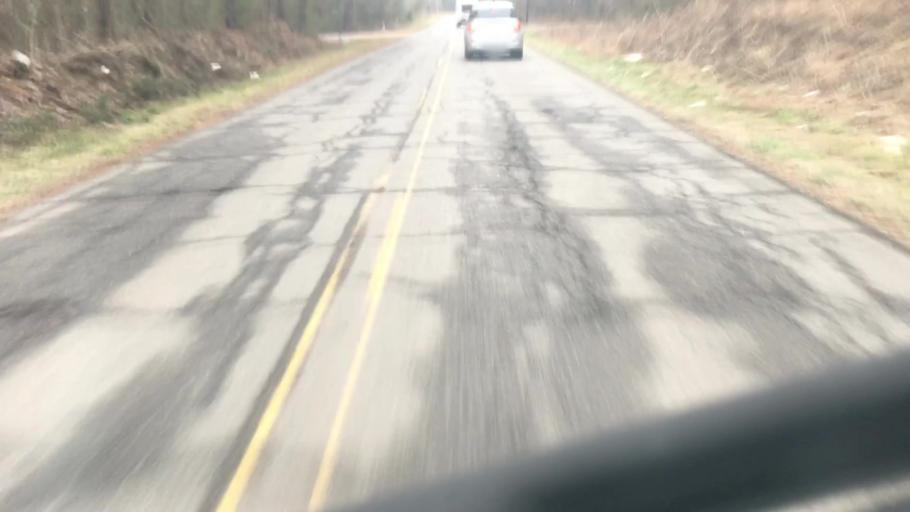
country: US
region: Alabama
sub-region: Walker County
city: Jasper
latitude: 33.8248
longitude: -87.2260
